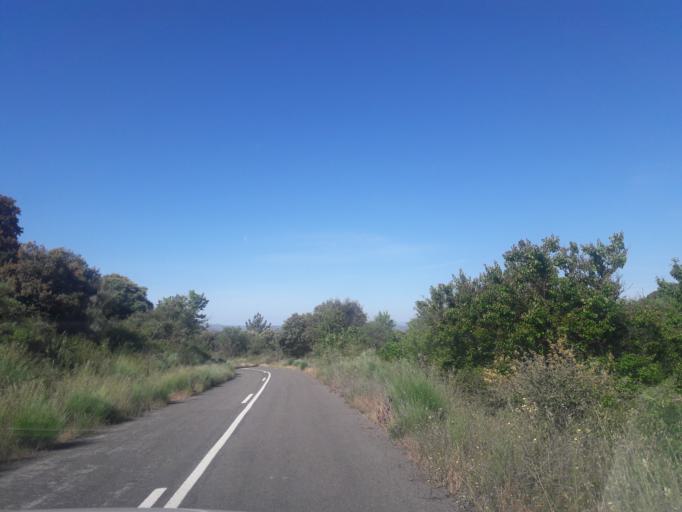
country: ES
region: Castille and Leon
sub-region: Provincia de Salamanca
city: Saucelle
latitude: 41.0364
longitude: -6.7665
